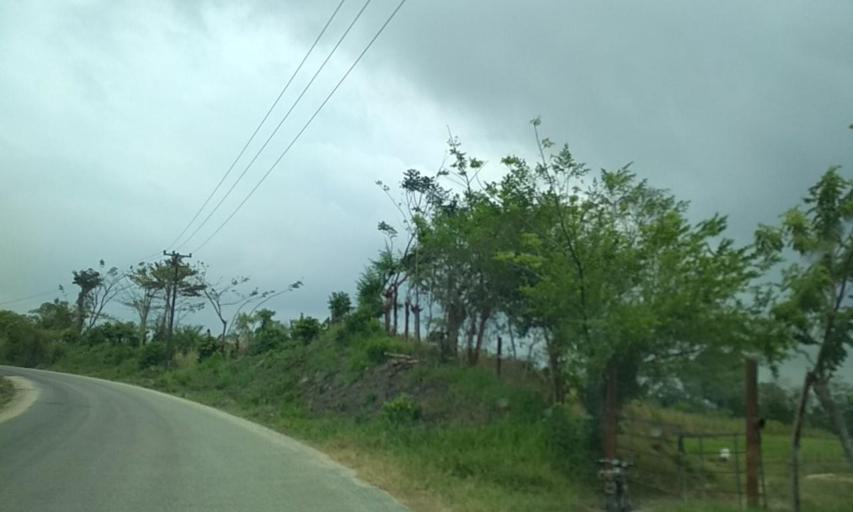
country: MX
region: Tabasco
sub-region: Huimanguillo
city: Francisco Rueda
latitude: 17.6008
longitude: -94.0901
